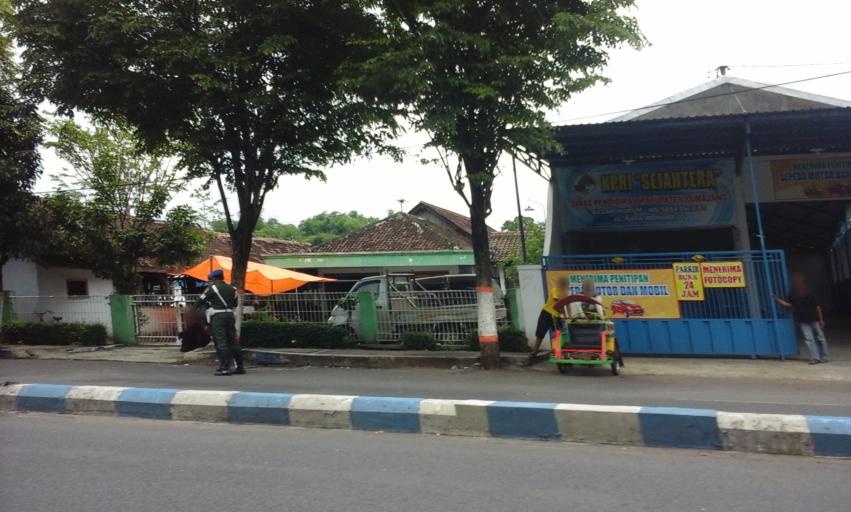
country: ID
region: East Java
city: Krajan
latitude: -8.0749
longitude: 113.2367
